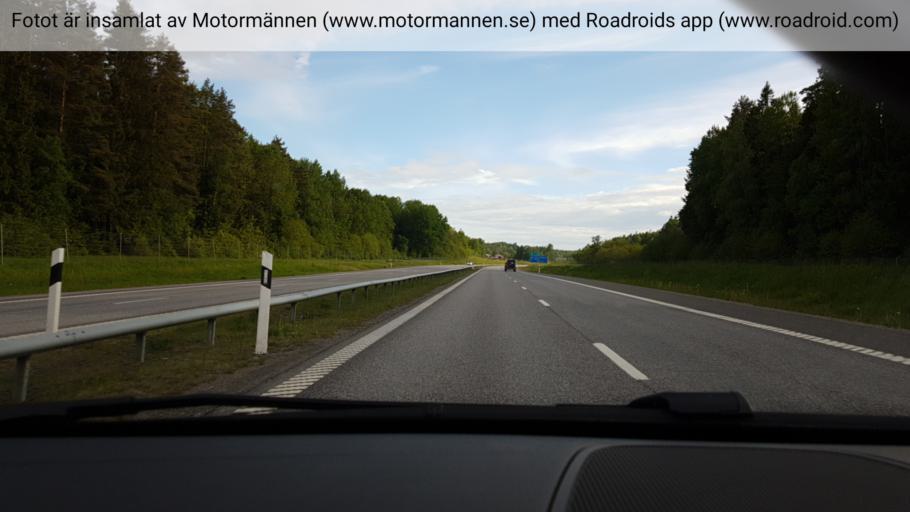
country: SE
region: Stockholm
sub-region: Nynashamns Kommun
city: Osmo
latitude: 59.0060
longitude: 17.9412
